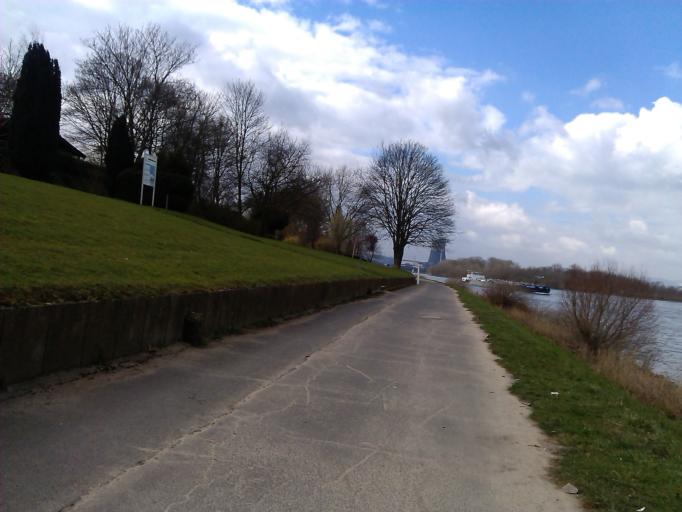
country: DE
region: Rheinland-Pfalz
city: Urmitz
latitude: 50.4193
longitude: 7.5256
